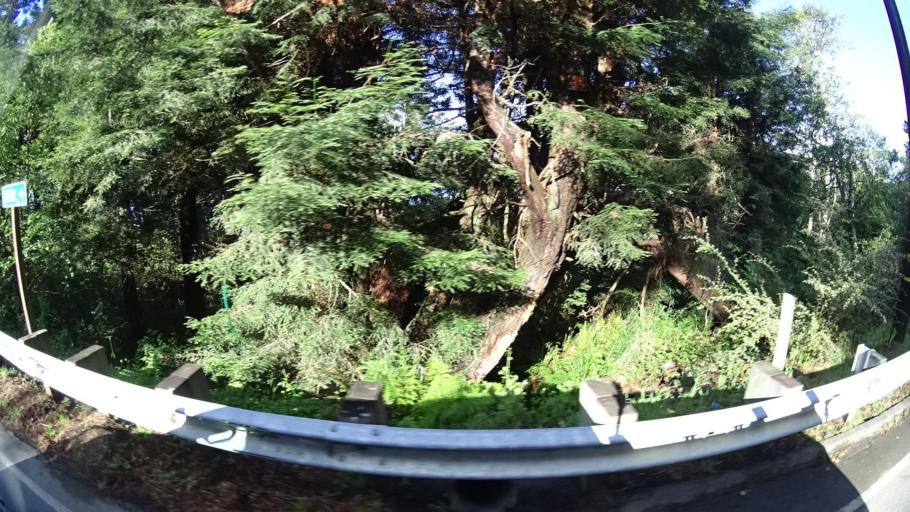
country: US
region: California
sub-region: Humboldt County
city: Westhaven-Moonstone
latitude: 41.0535
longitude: -124.1301
